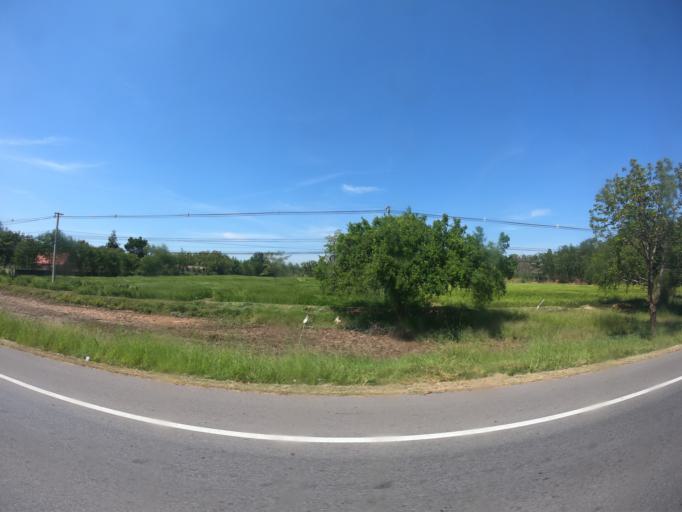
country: TH
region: Khon Kaen
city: Phon
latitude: 15.8442
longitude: 102.6145
